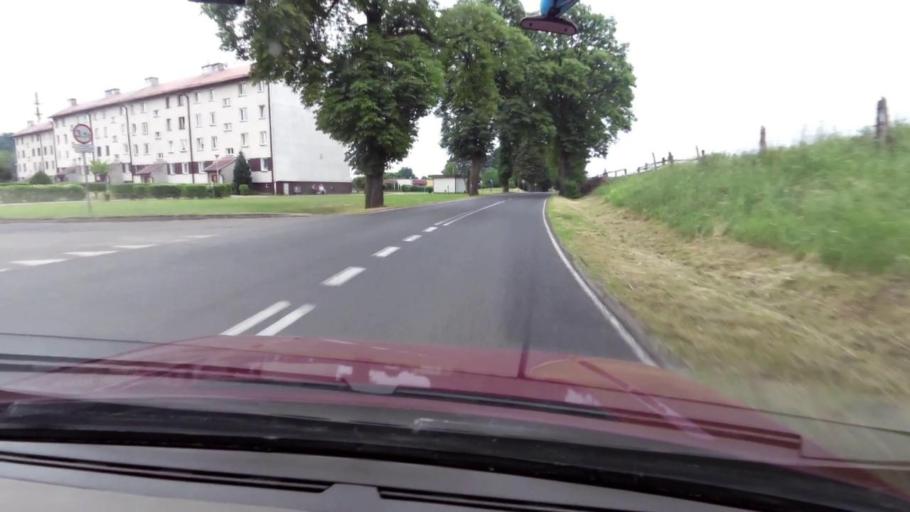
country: PL
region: West Pomeranian Voivodeship
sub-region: Powiat koszalinski
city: Polanow
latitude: 54.1251
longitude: 16.6822
